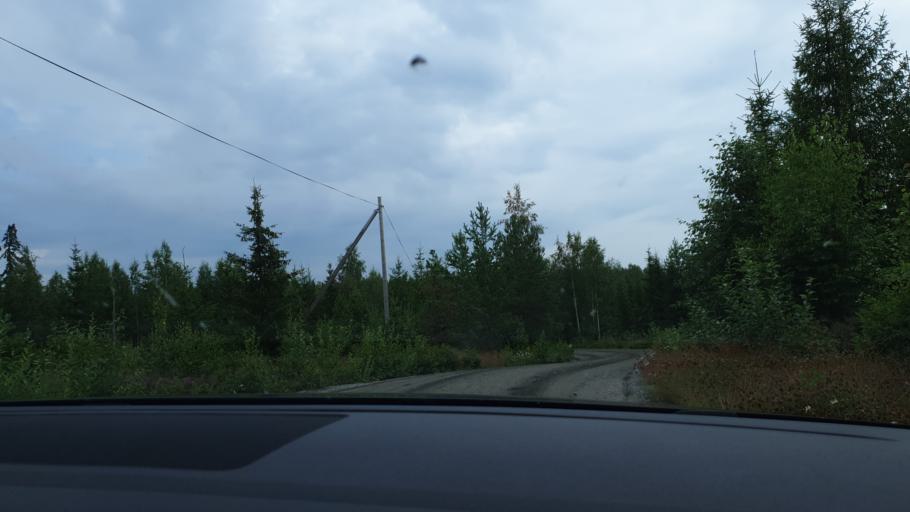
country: SE
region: Gaevleborg
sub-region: Hudiksvalls Kommun
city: Iggesund
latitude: 61.5269
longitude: 17.0130
